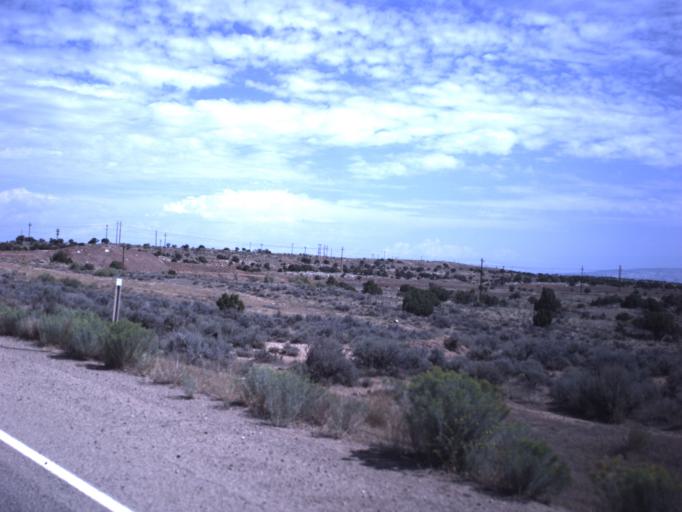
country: US
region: Utah
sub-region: Uintah County
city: Naples
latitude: 40.1798
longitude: -109.3238
